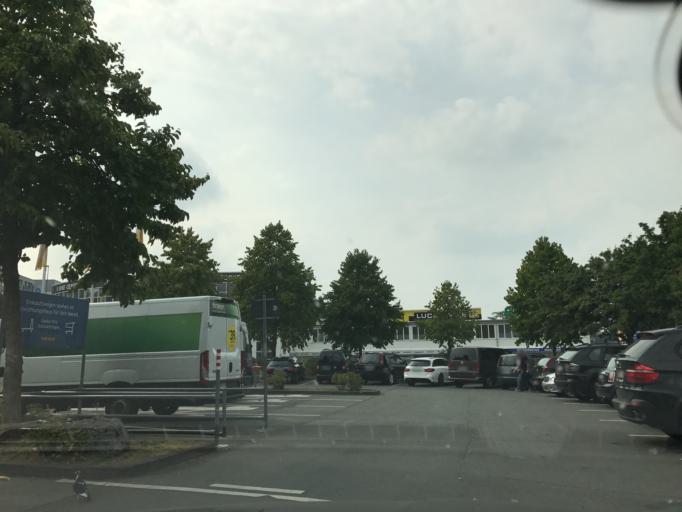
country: DE
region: North Rhine-Westphalia
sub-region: Regierungsbezirk Dusseldorf
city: Essen
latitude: 51.4592
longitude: 7.0006
